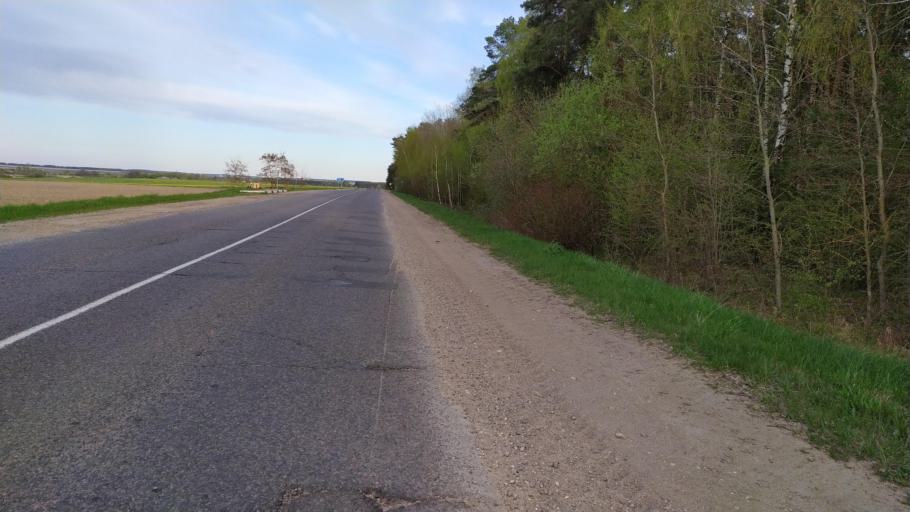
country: BY
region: Brest
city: Kamyanyets
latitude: 52.4169
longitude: 23.7000
